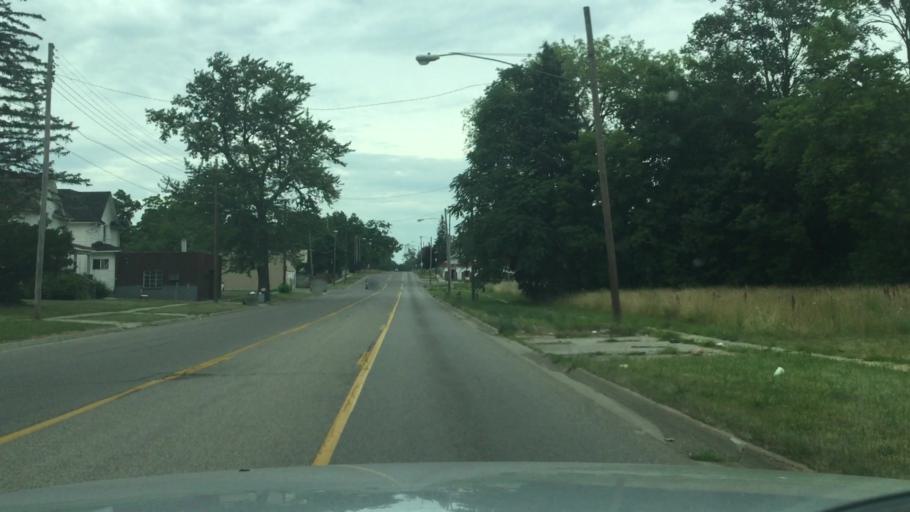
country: US
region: Michigan
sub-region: Genesee County
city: Flint
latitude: 43.0255
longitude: -83.6988
